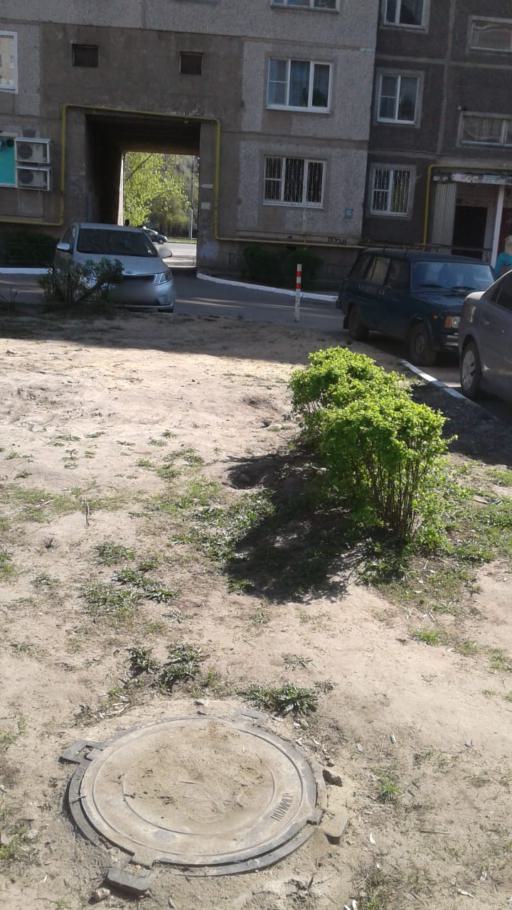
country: RU
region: Voronezj
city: Podgornoye
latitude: 51.7135
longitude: 39.1720
